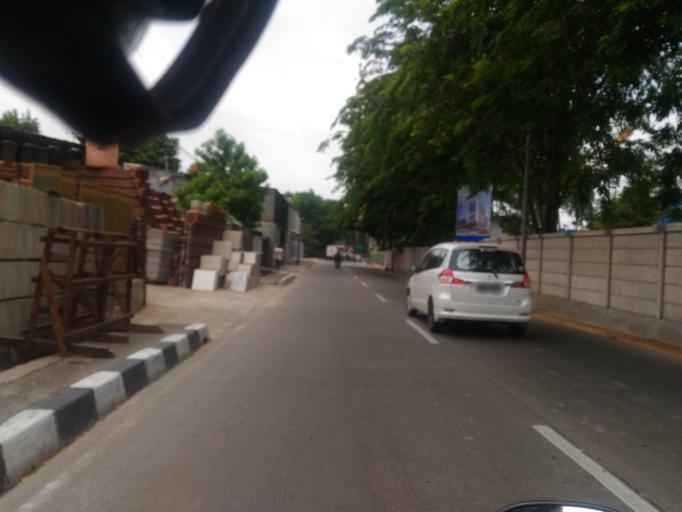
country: ID
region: West Java
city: Depok
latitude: -6.3107
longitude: 106.8382
